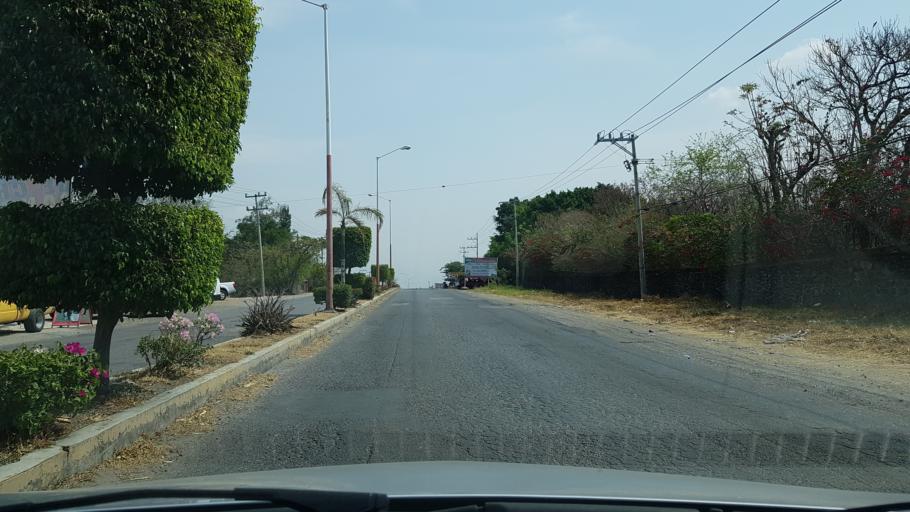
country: MX
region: Morelos
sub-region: Xochitepec
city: Chiconcuac
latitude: 18.7931
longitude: -99.2019
